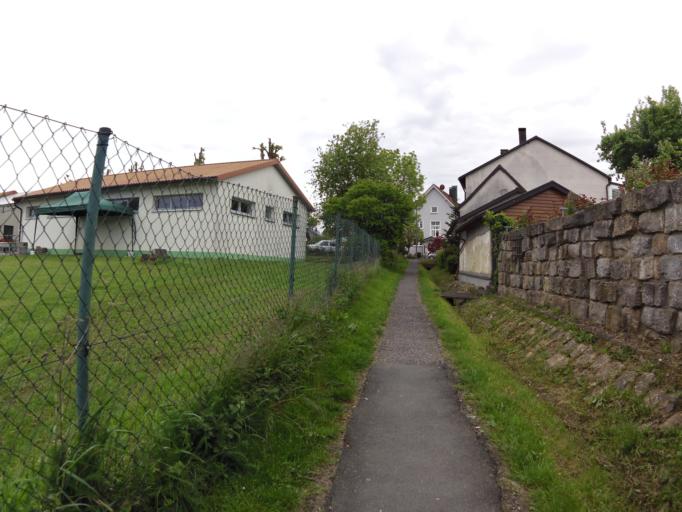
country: DE
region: Bavaria
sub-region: Regierungsbezirk Unterfranken
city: Kurnach
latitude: 49.8442
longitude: 10.0447
